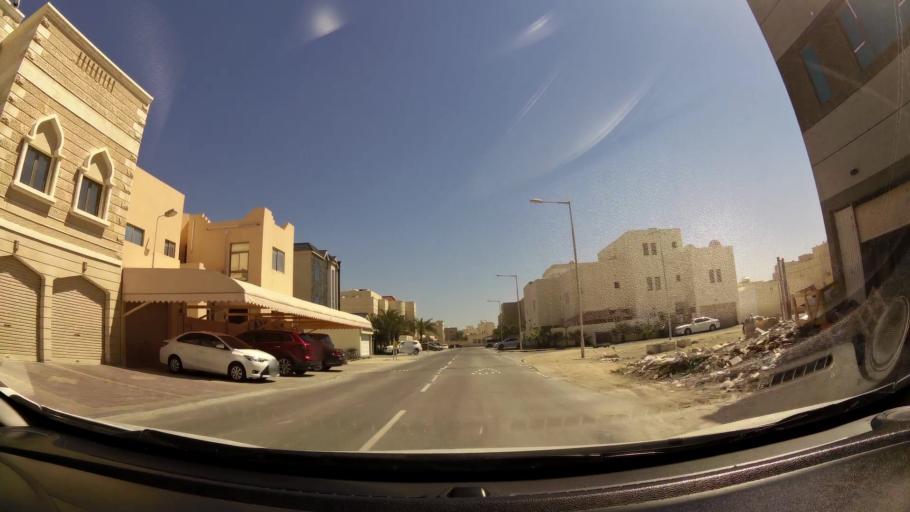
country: BH
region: Muharraq
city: Al Muharraq
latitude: 26.2747
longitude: 50.6013
